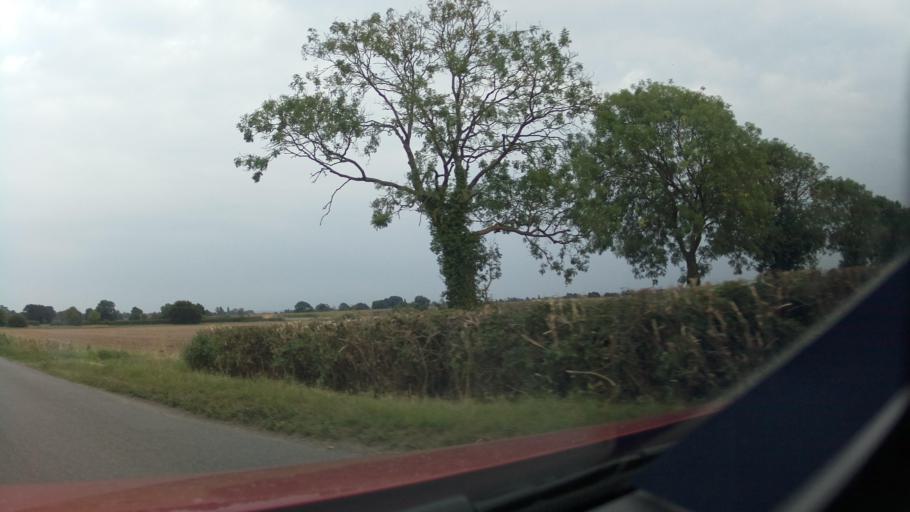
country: GB
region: England
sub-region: Lincolnshire
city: Skellingthorpe
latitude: 53.1429
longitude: -0.6598
